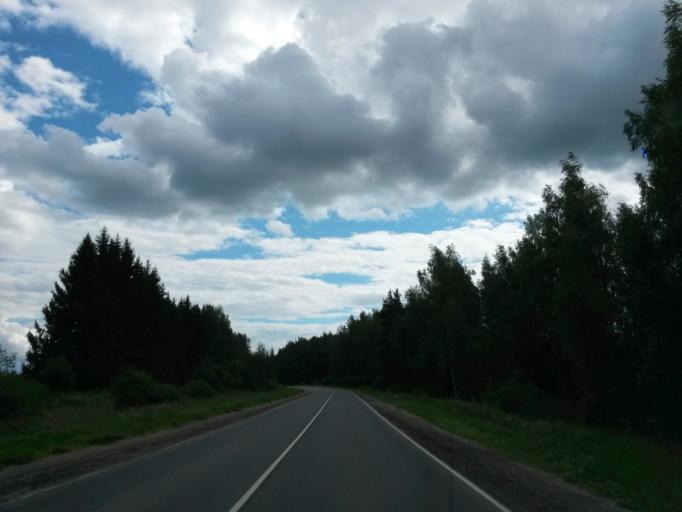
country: RU
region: Ivanovo
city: Pistsovo
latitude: 57.0929
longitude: 40.6619
